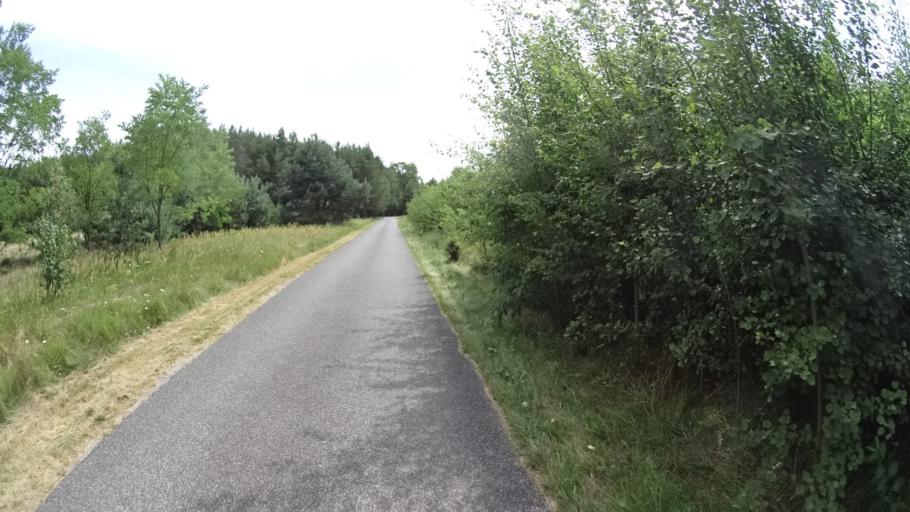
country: PL
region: Masovian Voivodeship
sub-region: Powiat bialobrzeski
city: Bialobrzegi
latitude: 51.6424
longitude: 20.9026
